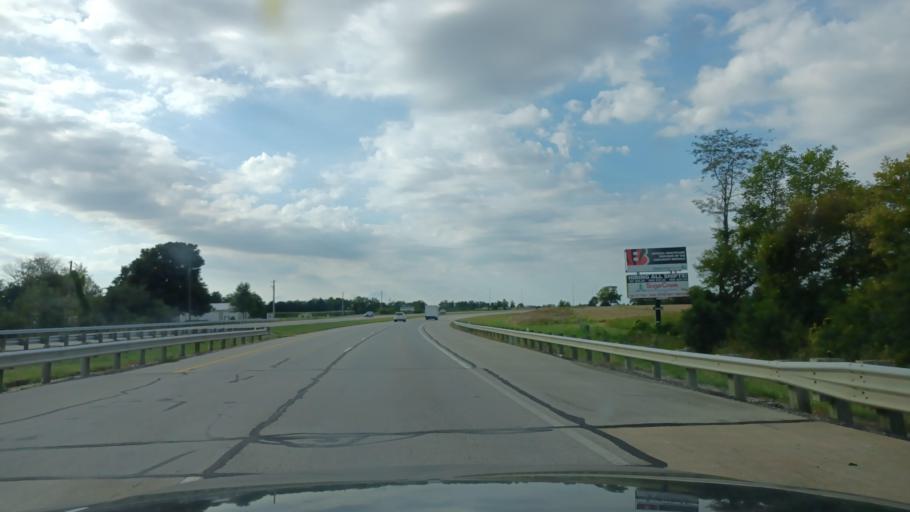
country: US
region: Ohio
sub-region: Fayette County
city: Jeffersonville
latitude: 39.6238
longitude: -83.6163
